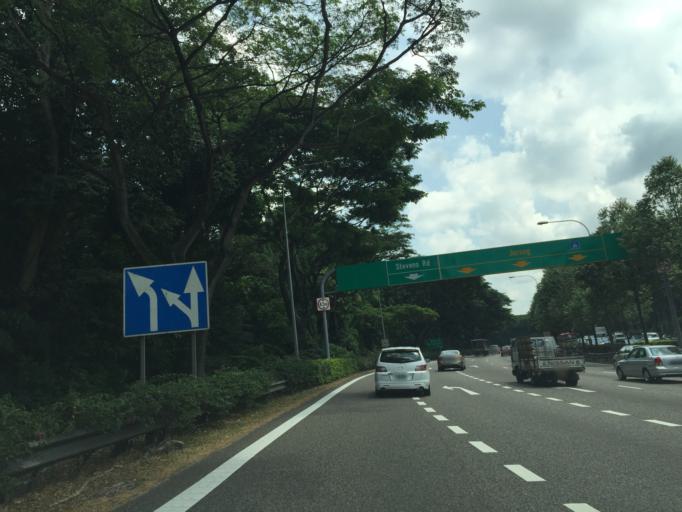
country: SG
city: Singapore
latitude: 1.3257
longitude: 103.8321
